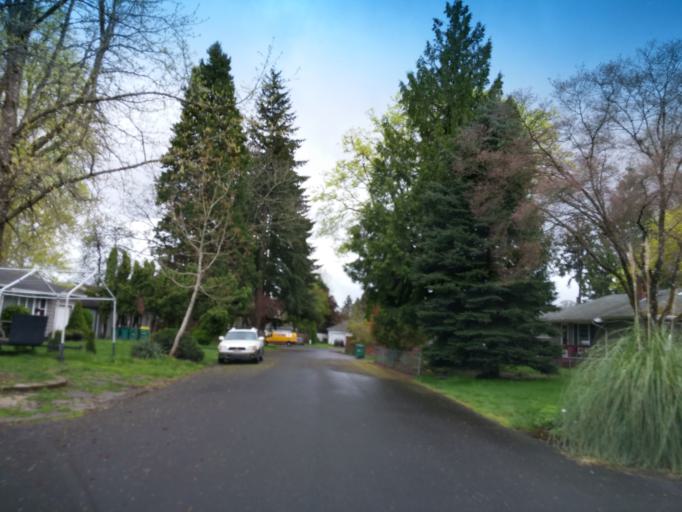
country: US
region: Oregon
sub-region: Washington County
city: Cedar Mill
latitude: 45.5185
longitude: -122.8197
